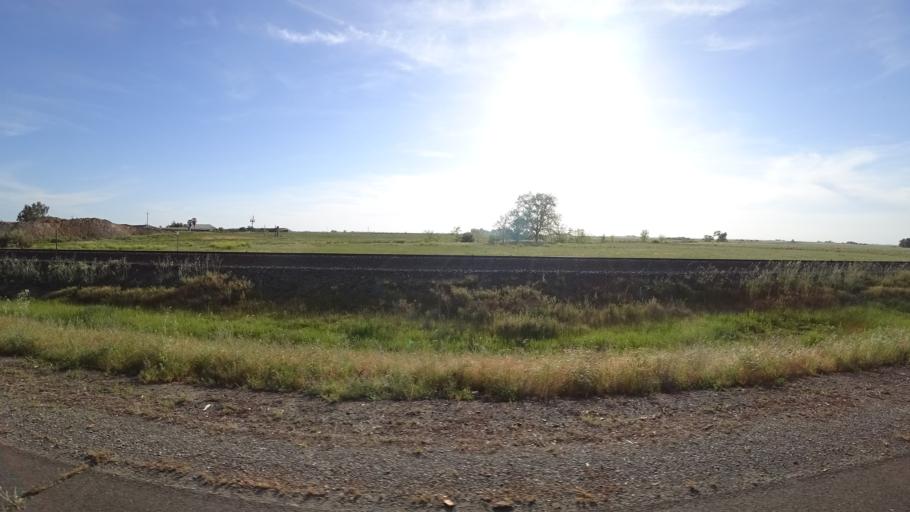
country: US
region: California
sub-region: Placer County
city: Sheridan
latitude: 38.9571
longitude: -121.3567
